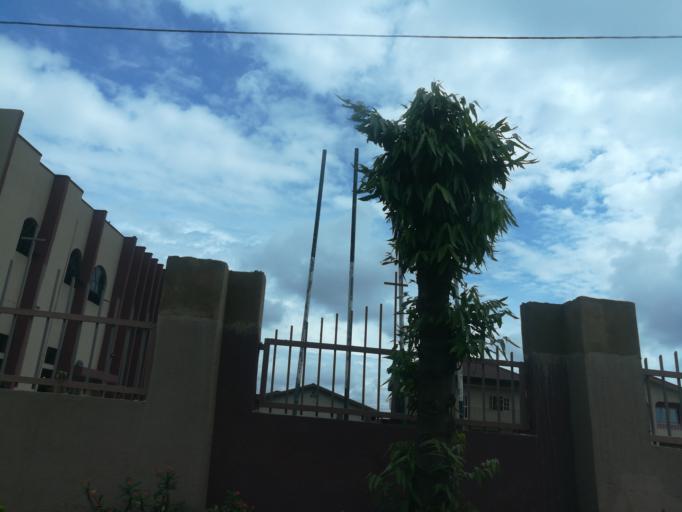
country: NG
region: Lagos
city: Agege
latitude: 6.6252
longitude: 3.3323
